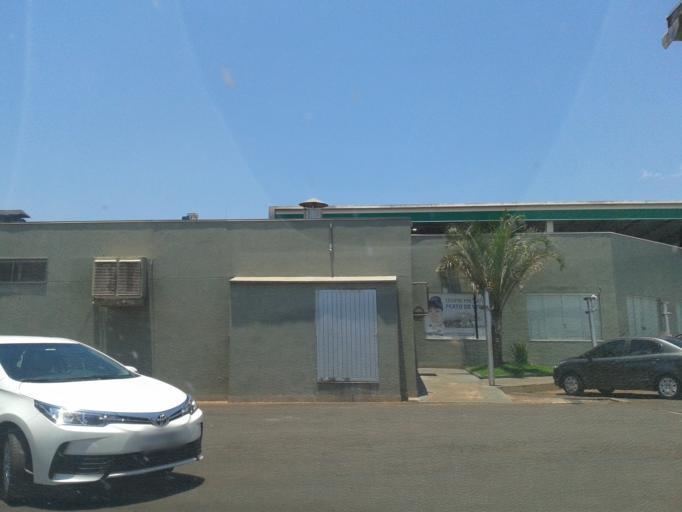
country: BR
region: Goias
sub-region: Itumbiara
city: Itumbiara
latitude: -18.4250
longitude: -49.1924
